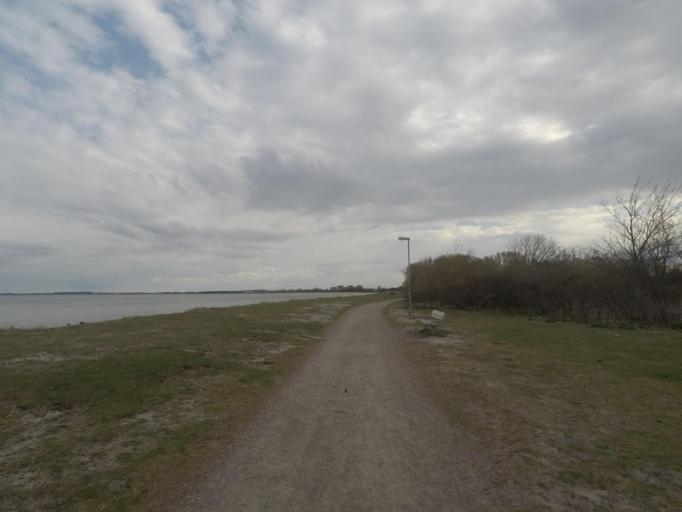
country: SE
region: Skane
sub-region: Lomma Kommun
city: Lomma
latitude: 55.6587
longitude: 13.0560
